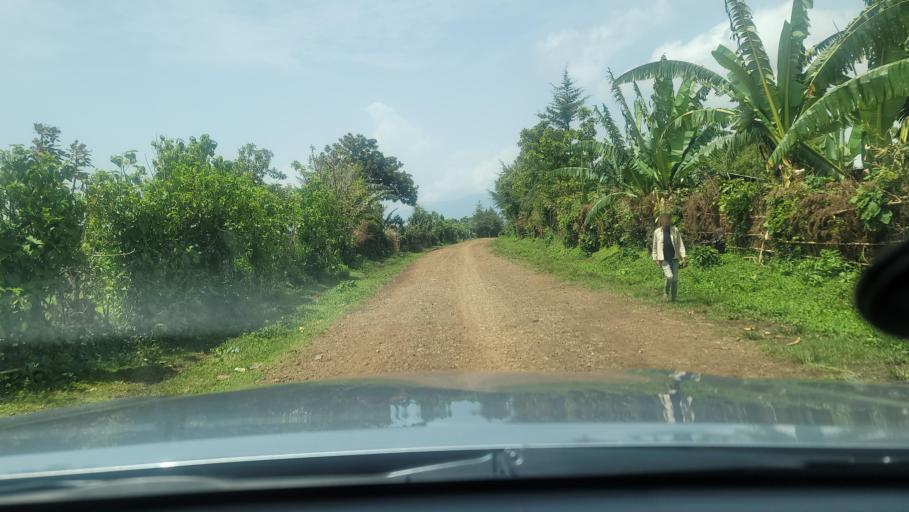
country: ET
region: Oromiya
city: Agaro
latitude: 7.8311
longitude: 36.4067
